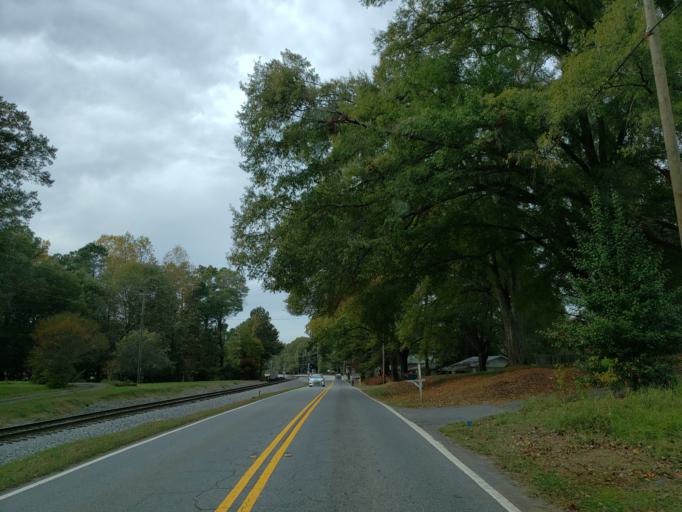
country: US
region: Georgia
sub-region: Cobb County
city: Acworth
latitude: 34.0634
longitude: -84.6582
